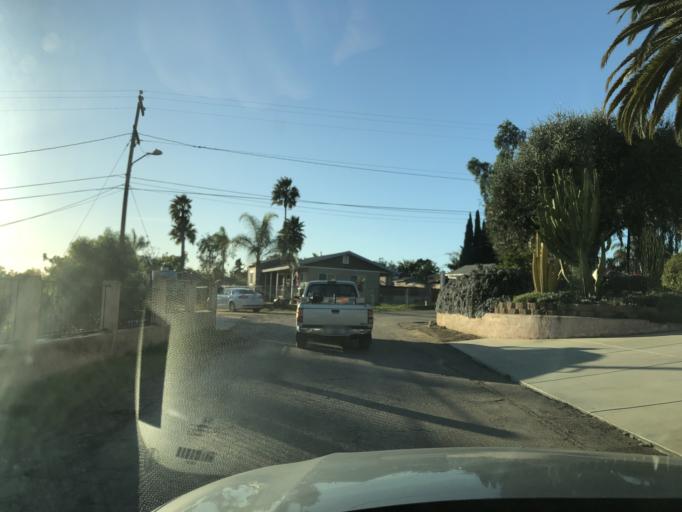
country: US
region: California
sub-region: San Diego County
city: Chula Vista
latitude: 32.6524
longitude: -117.0589
